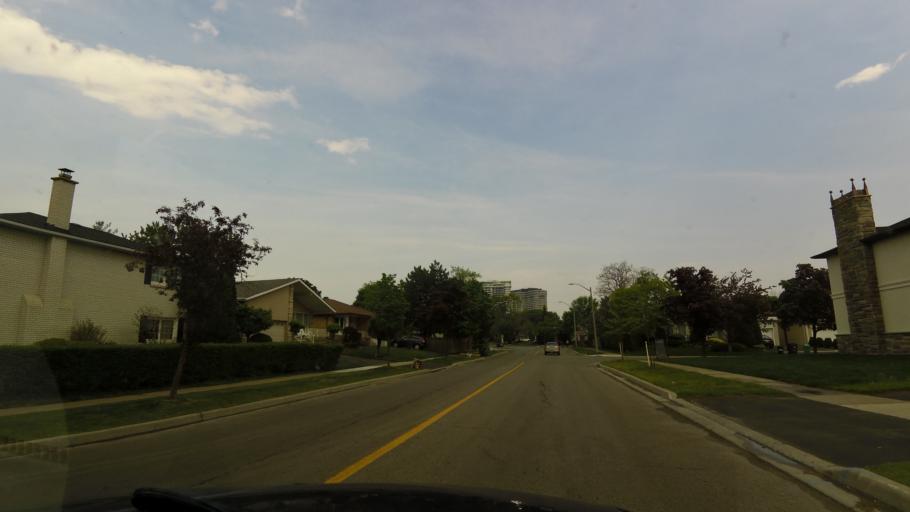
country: CA
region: Ontario
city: Etobicoke
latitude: 43.6166
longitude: -79.6035
